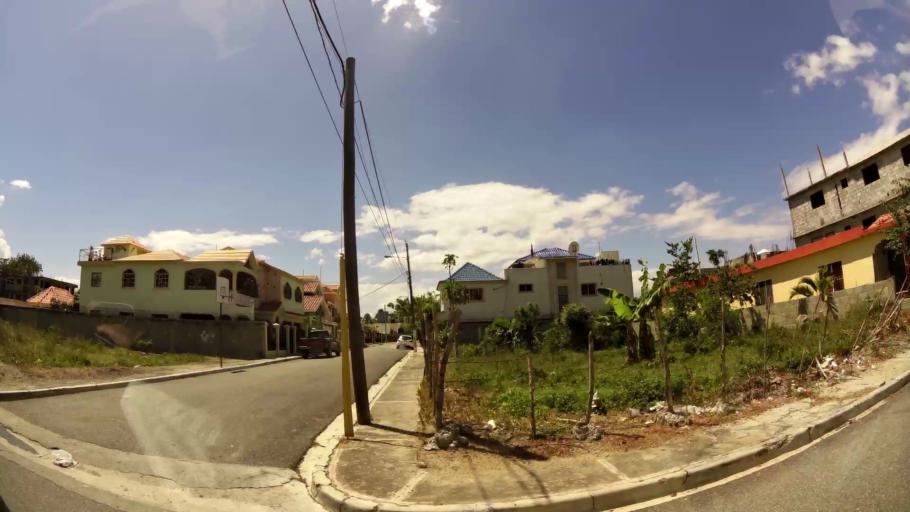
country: DO
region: San Cristobal
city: San Cristobal
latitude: 18.4128
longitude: -70.0917
